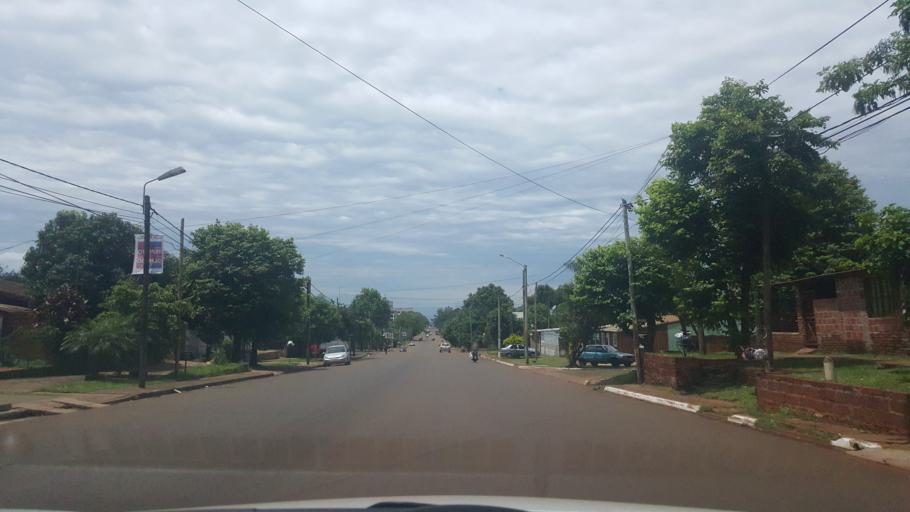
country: AR
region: Misiones
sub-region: Departamento de Capital
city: Posadas
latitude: -27.3784
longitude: -55.9231
